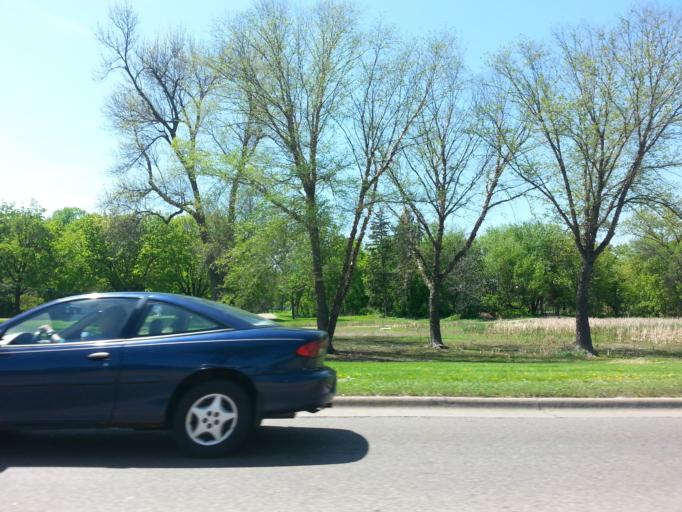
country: US
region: Minnesota
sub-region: Hennepin County
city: Richfield
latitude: 44.9019
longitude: -93.2475
